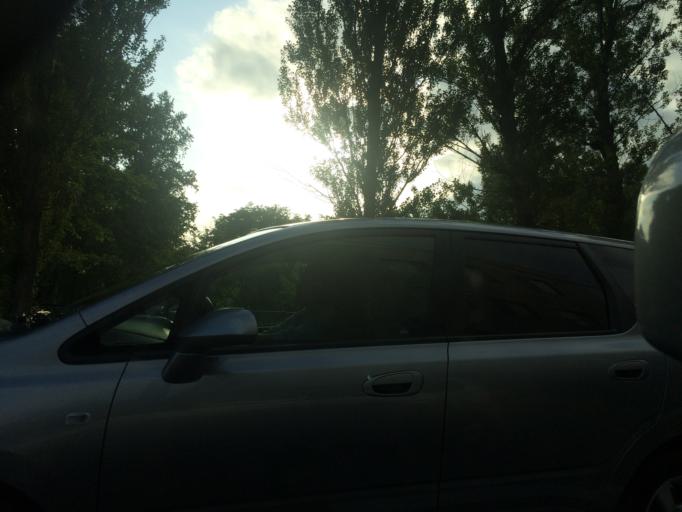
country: JP
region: Hokkaido
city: Sapporo
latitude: 42.9967
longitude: 141.3492
